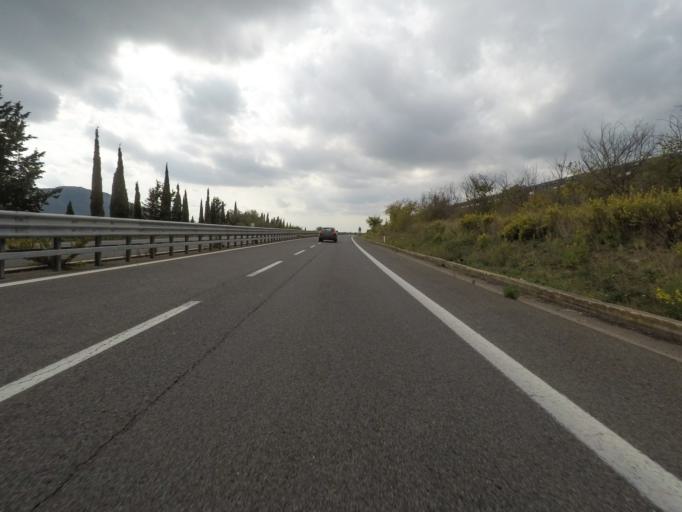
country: IT
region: Tuscany
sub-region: Provincia di Grosseto
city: Bagno Roselle
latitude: 42.8390
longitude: 11.1512
